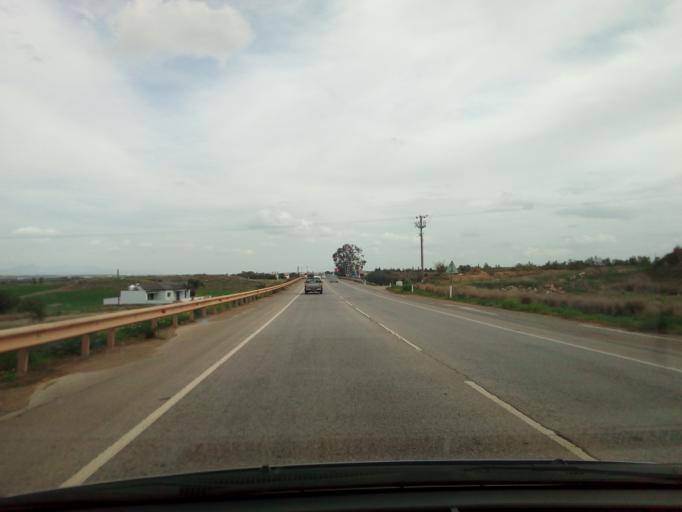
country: CY
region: Lefkosia
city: Akaki
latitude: 35.1354
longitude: 33.1074
